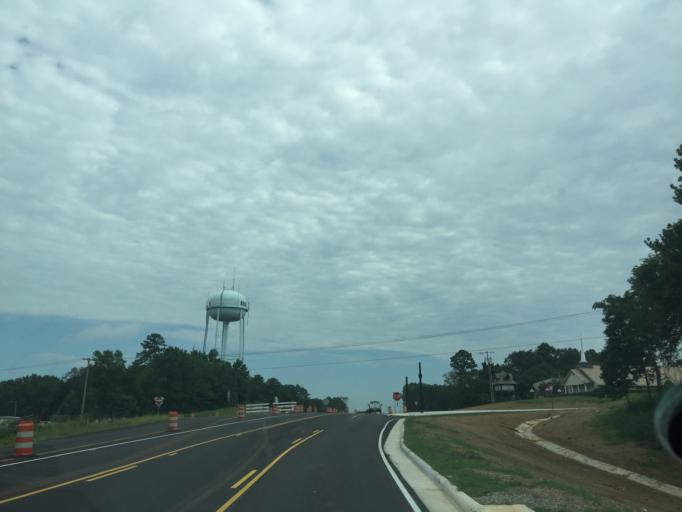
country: US
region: Mississippi
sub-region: Rankin County
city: Brandon
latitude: 32.2761
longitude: -89.9938
